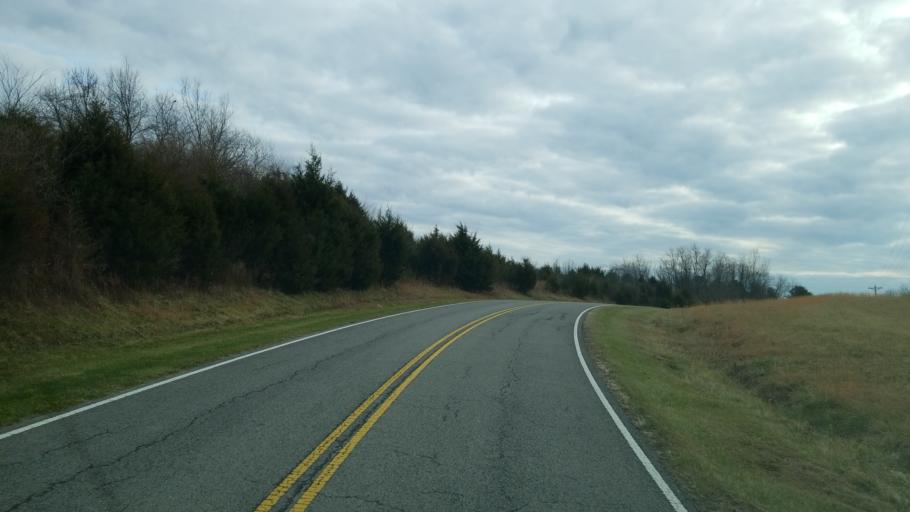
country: US
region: Ohio
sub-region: Highland County
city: Greenfield
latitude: 39.2332
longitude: -83.3884
